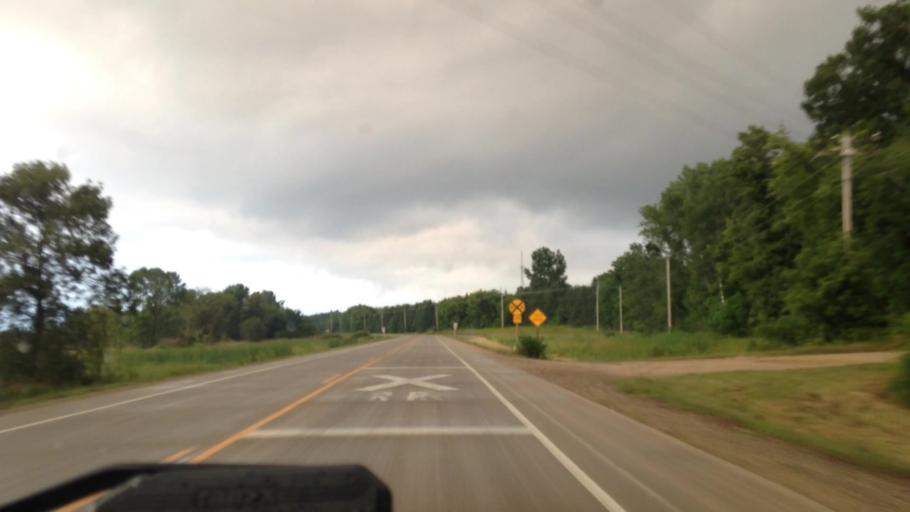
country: US
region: Wisconsin
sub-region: Dodge County
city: Mayville
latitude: 43.4729
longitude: -88.5571
